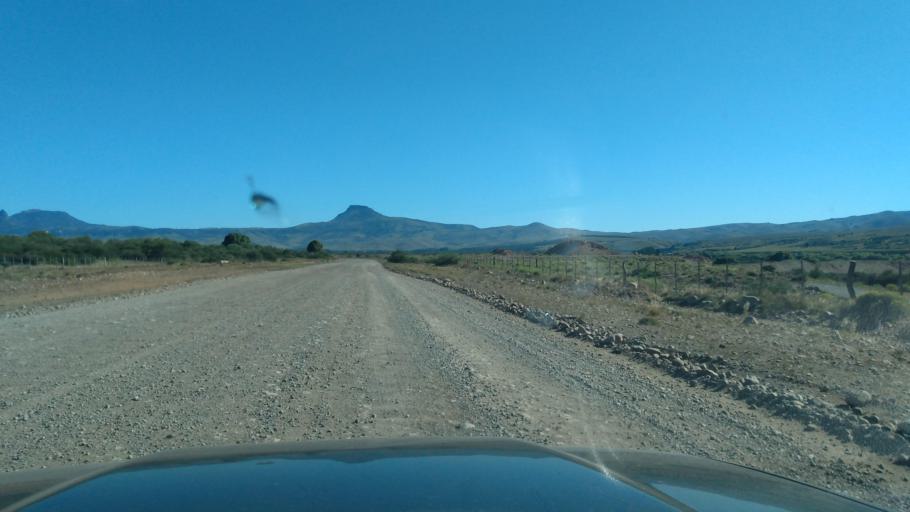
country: AR
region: Neuquen
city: Junin de los Andes
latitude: -39.8532
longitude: -71.1875
